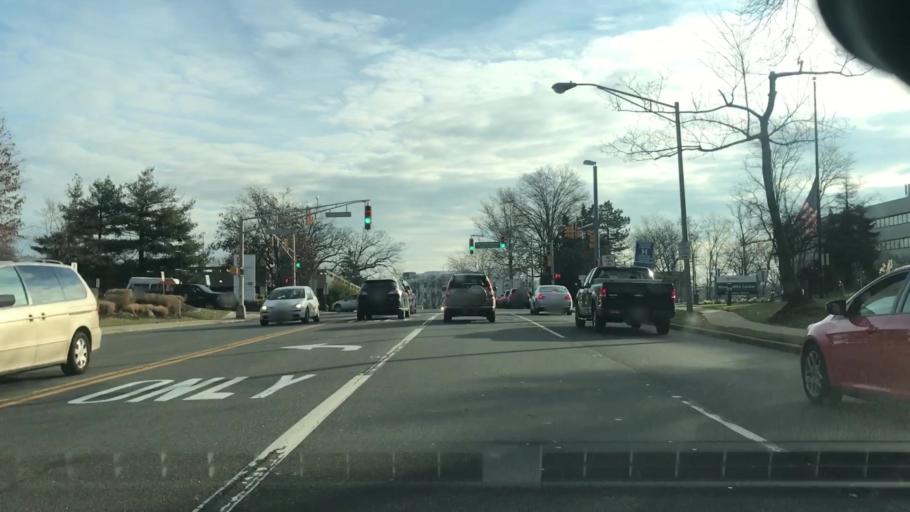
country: US
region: New Jersey
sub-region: Morris County
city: Morristown
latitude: 40.7881
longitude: -74.4661
